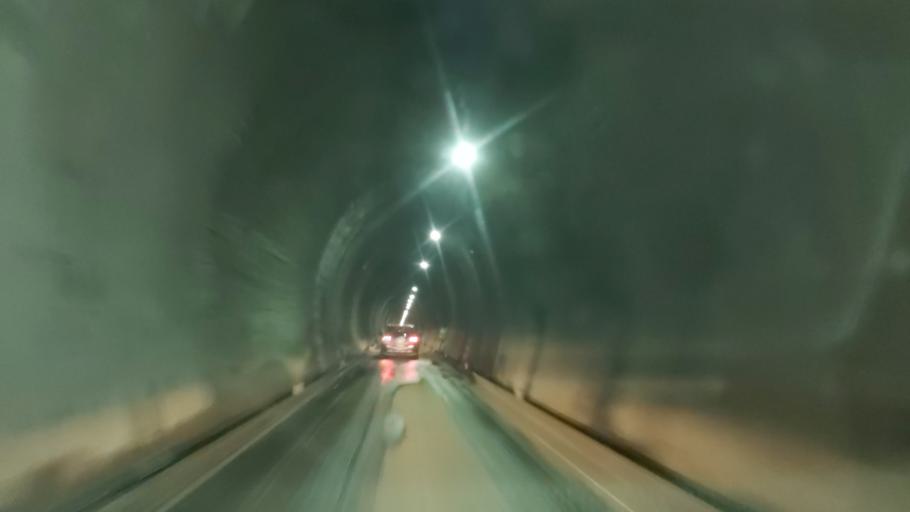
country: CL
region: Araucania
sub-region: Provincia de Cautin
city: Vilcun
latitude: -38.5279
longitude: -71.5119
